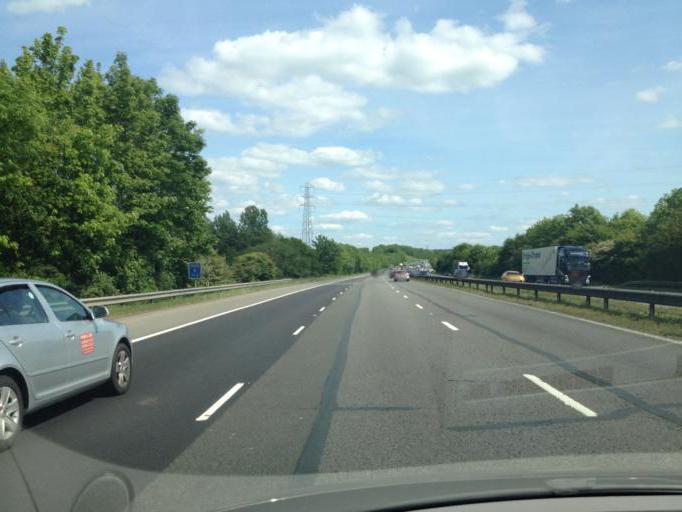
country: GB
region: England
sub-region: Oxfordshire
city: Thame
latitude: 51.7050
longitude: -1.0017
